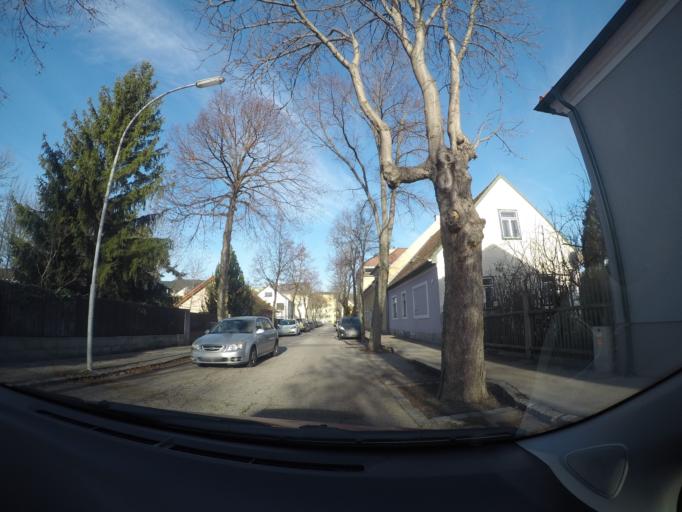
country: AT
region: Lower Austria
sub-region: Politischer Bezirk Baden
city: Baden
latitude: 48.0032
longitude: 16.2210
